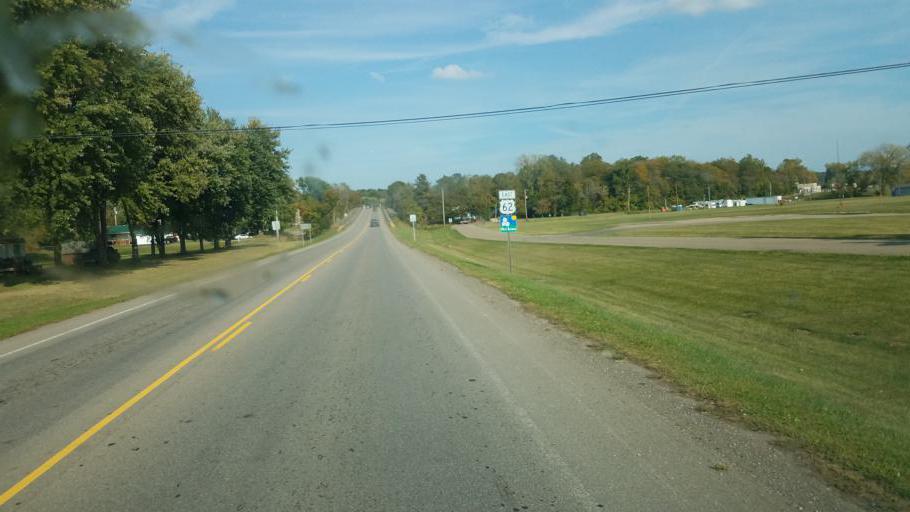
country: US
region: Ohio
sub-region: Licking County
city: Utica
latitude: 40.2299
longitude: -82.4517
